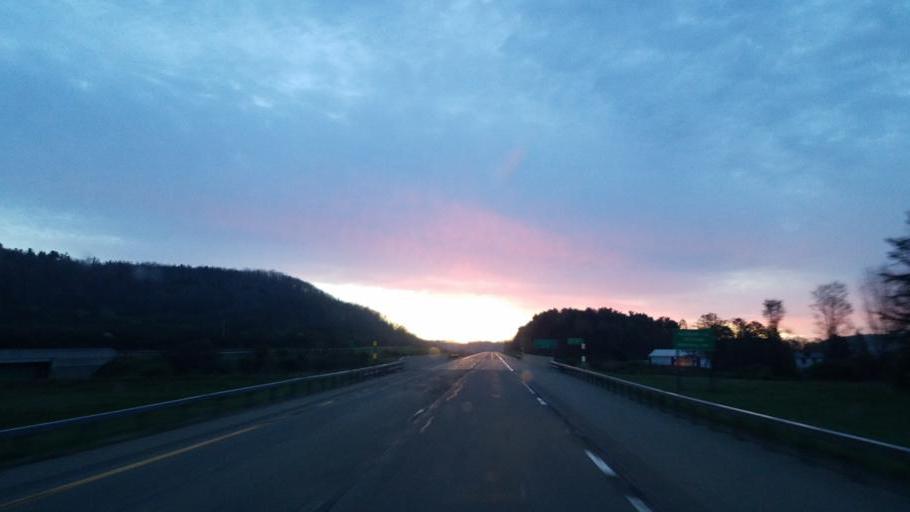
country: US
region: New York
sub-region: Allegany County
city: Cuba
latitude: 42.2175
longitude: -78.3023
